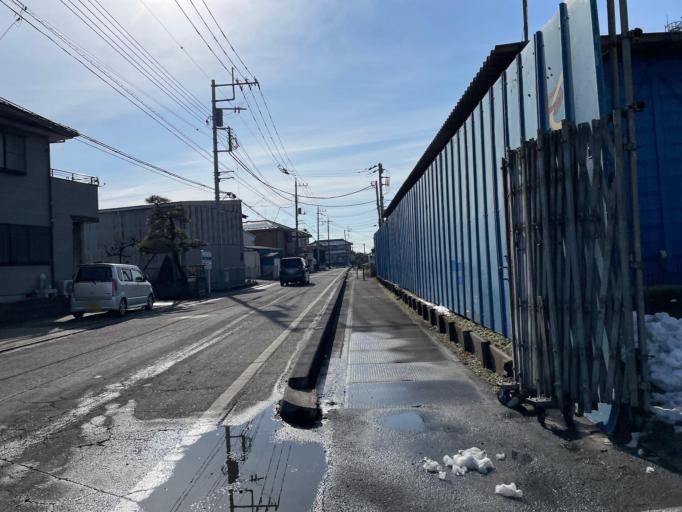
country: JP
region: Chiba
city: Nagareyama
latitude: 35.8618
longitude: 139.8754
